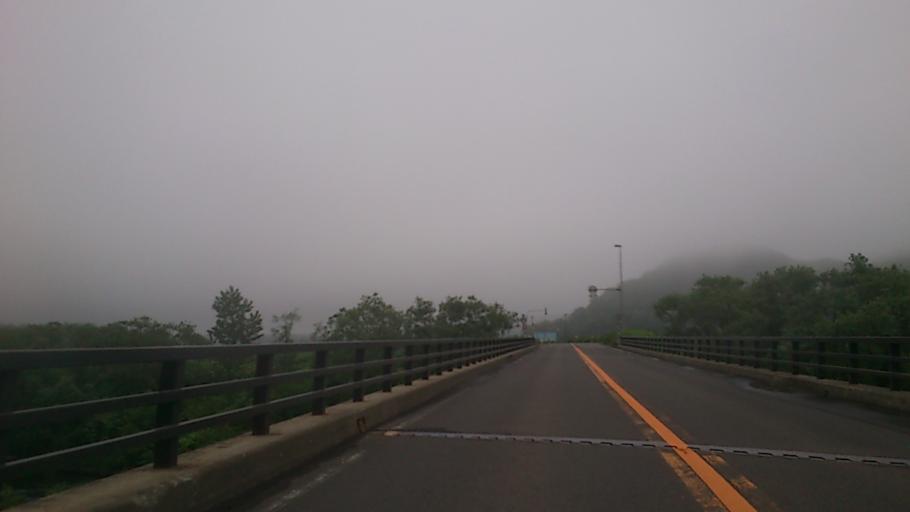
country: JP
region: Hokkaido
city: Niseko Town
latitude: 42.8116
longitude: 140.8883
